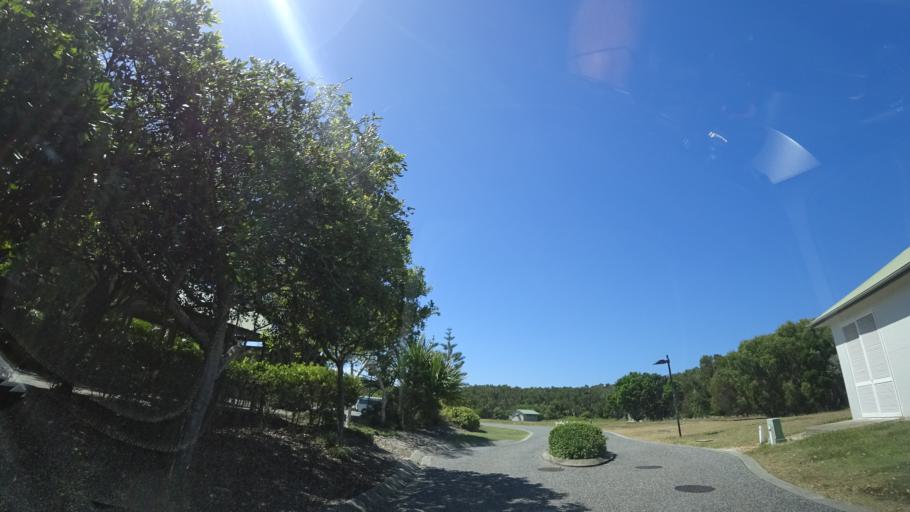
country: AU
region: Queensland
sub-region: Sunshine Coast
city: Mooloolaba
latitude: -26.6320
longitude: 153.0999
